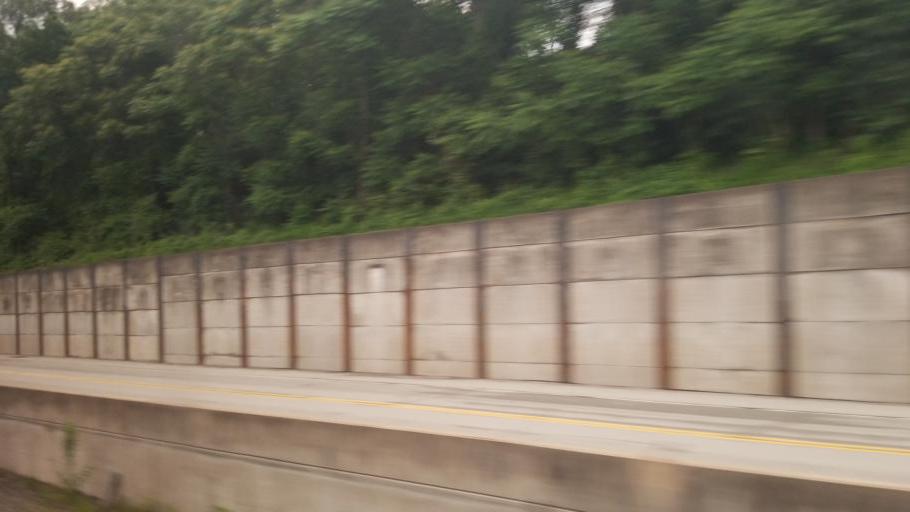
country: US
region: Pennsylvania
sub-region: Allegheny County
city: Bloomfield
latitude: 40.4561
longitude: -79.9728
